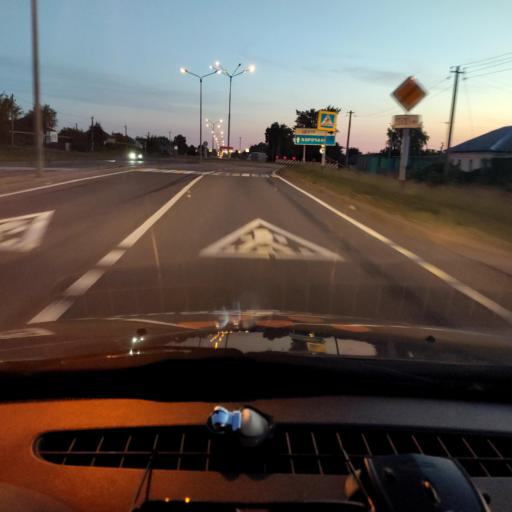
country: RU
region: Belgorod
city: Gubkin
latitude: 51.2703
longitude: 37.5742
